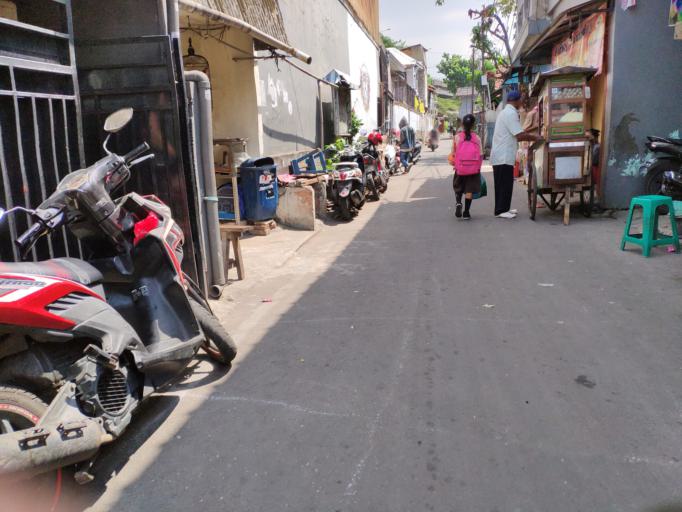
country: ID
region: Jakarta Raya
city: Jakarta
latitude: -6.1987
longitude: 106.8733
